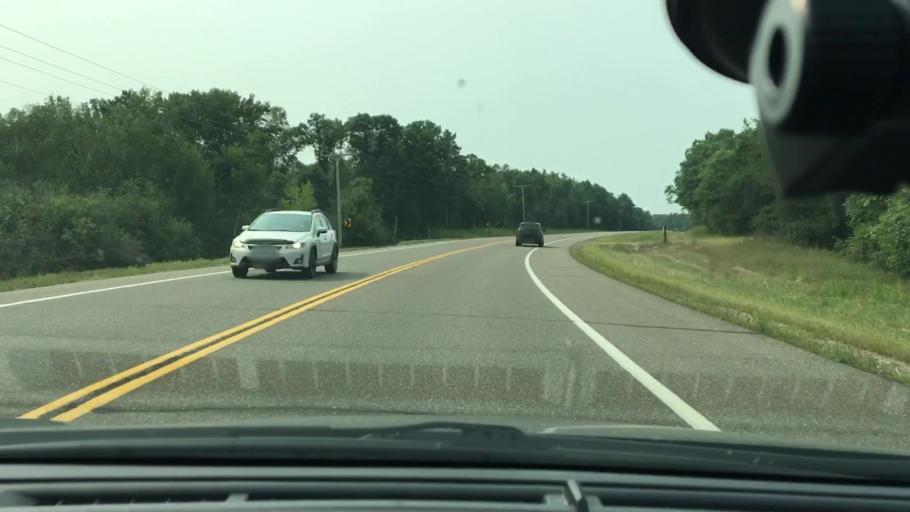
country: US
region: Minnesota
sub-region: Crow Wing County
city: Breezy Point
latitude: 46.5663
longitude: -94.1292
